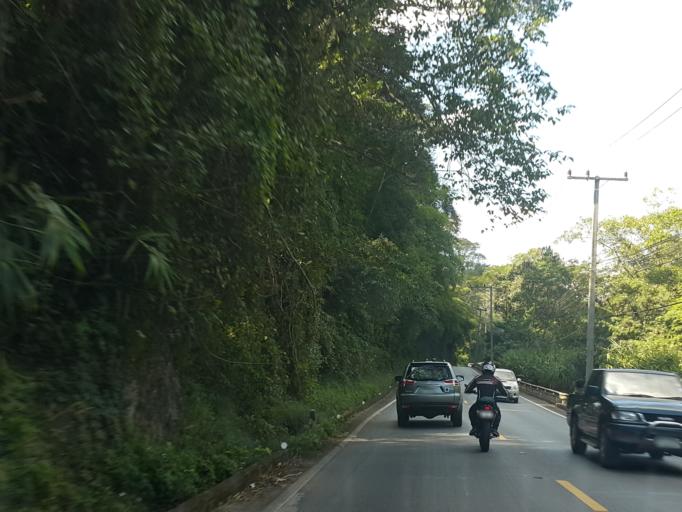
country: TH
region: Chiang Mai
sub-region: Amphoe Chiang Dao
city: Chiang Dao
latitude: 19.2969
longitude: 98.9613
